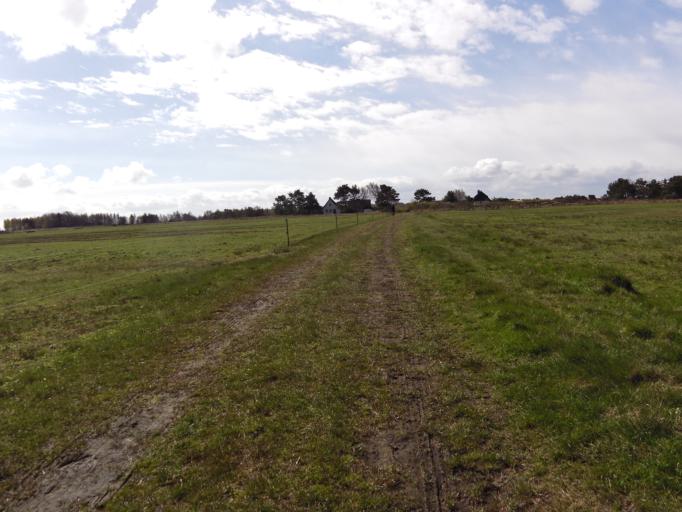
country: DE
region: Mecklenburg-Vorpommern
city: Hiddensee
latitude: 54.5562
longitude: 13.1037
